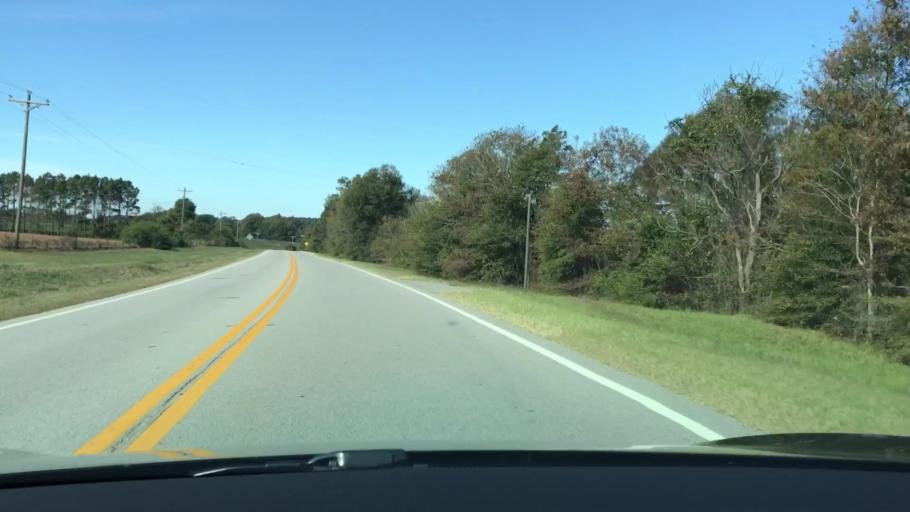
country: US
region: Georgia
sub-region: Glascock County
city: Gibson
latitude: 33.3180
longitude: -82.5496
